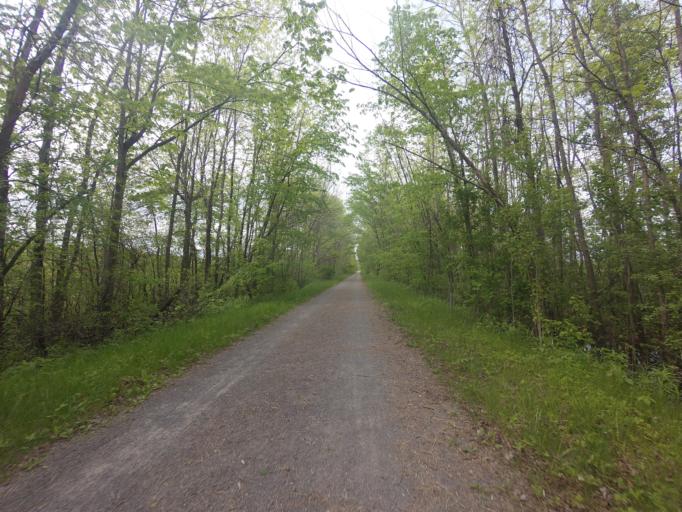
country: CA
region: Ontario
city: Kingston
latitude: 44.3190
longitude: -76.5866
